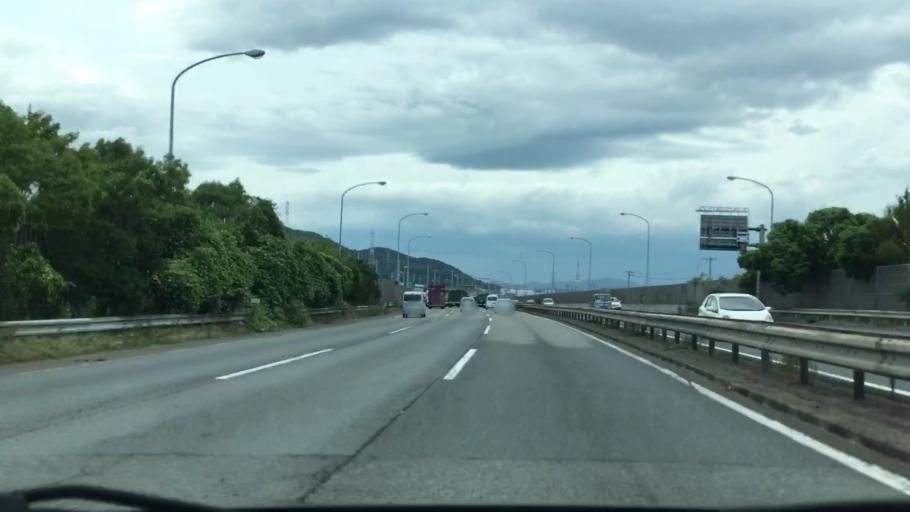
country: JP
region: Hyogo
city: Shirahamacho-usazakiminami
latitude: 34.7966
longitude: 134.7610
